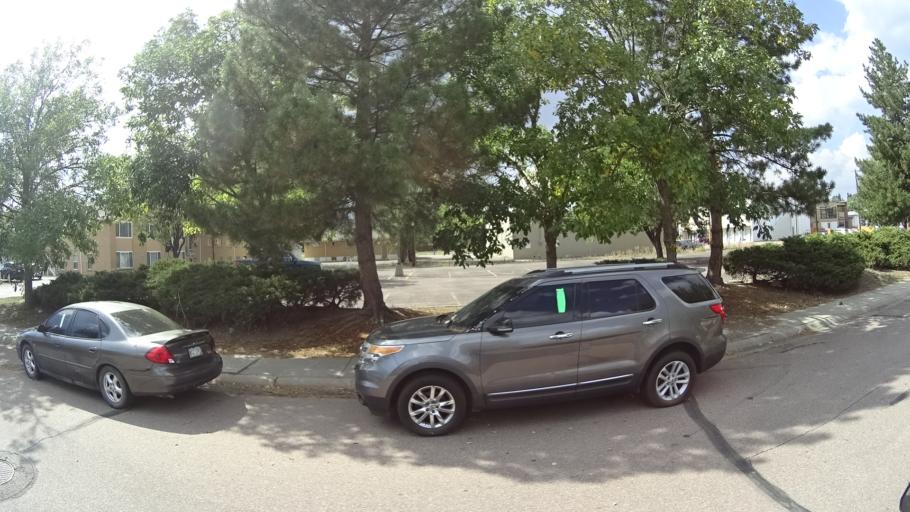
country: US
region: Colorado
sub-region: El Paso County
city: Colorado Springs
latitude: 38.8444
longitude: -104.7747
